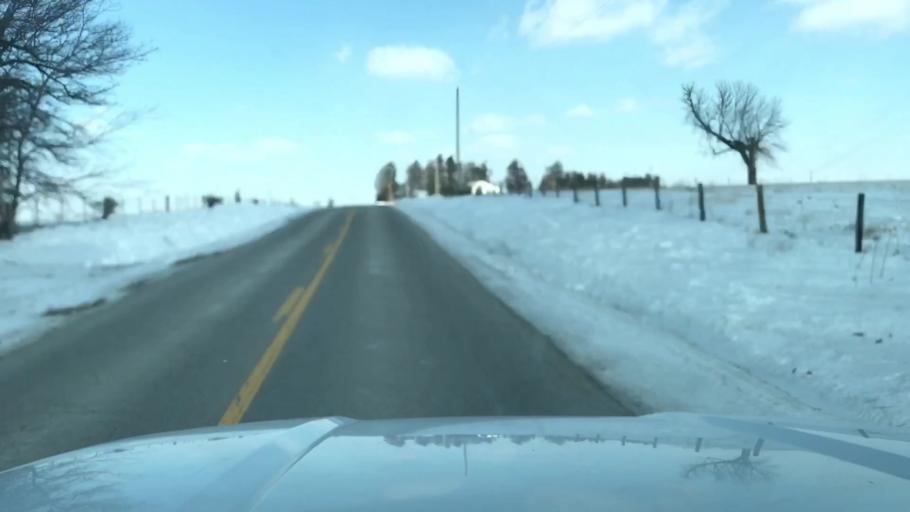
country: US
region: Missouri
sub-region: Nodaway County
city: Maryville
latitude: 40.3717
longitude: -94.7215
